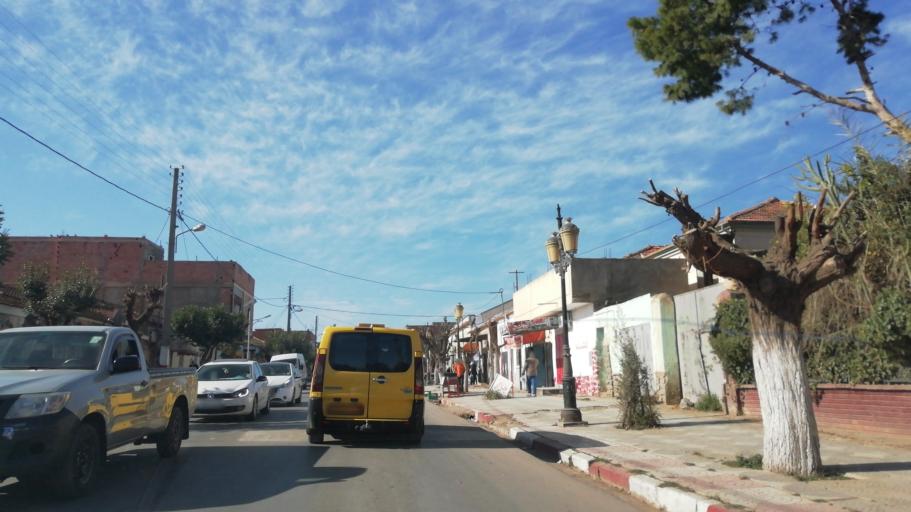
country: DZ
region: Tlemcen
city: Ouled Mimoun
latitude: 35.0263
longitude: -0.8877
